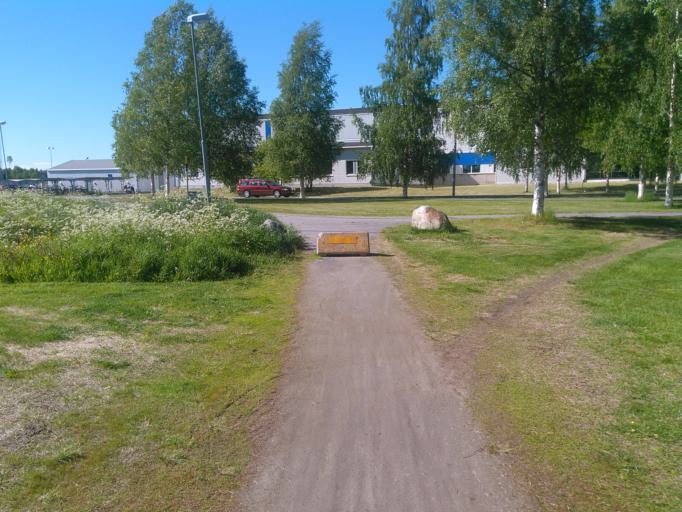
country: SE
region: Vaesterbotten
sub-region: Umea Kommun
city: Roback
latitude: 63.8197
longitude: 20.2053
